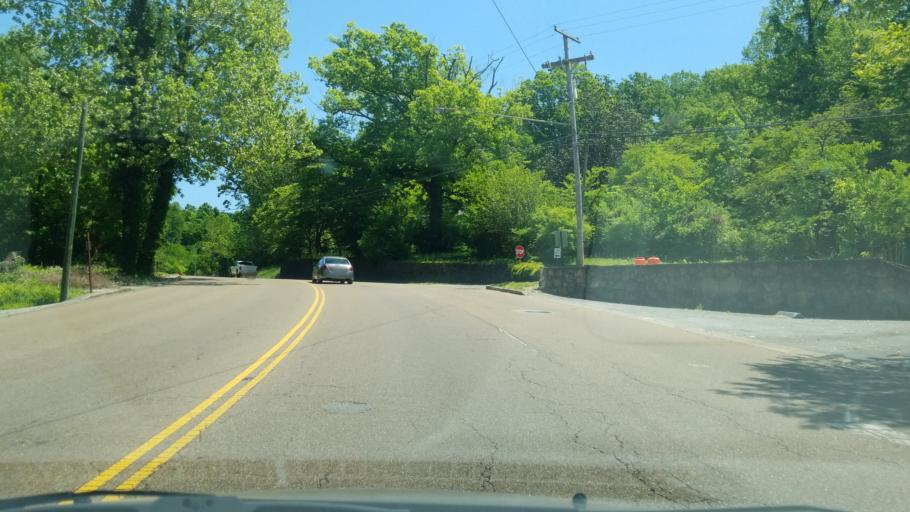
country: US
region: Tennessee
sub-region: Hamilton County
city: Red Bank
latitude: 35.1206
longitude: -85.2860
